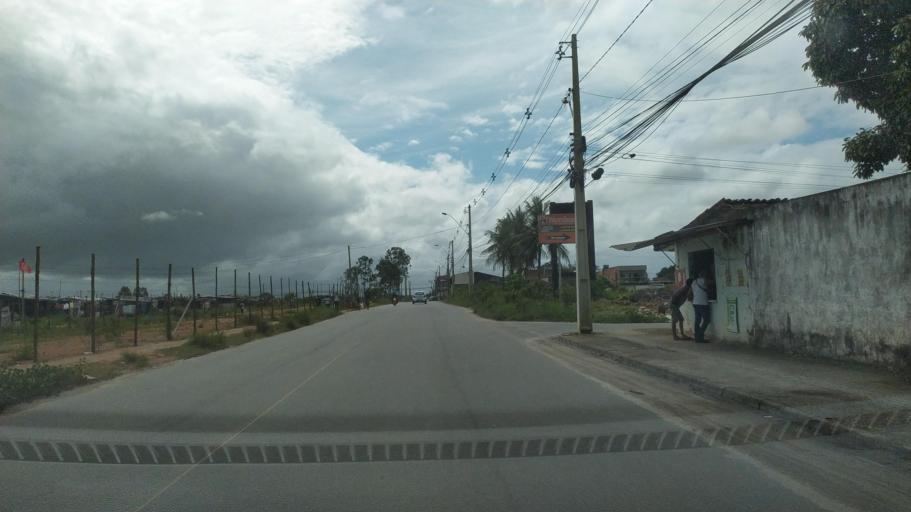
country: BR
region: Alagoas
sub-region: Satuba
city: Satuba
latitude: -9.5465
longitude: -35.7615
